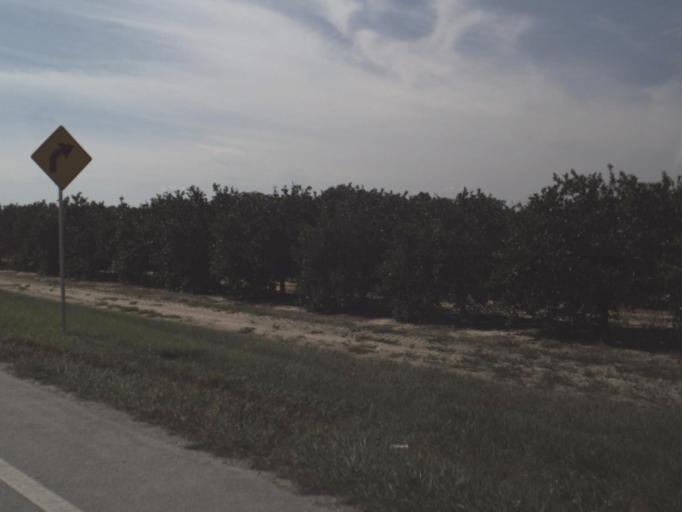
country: US
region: Florida
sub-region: Highlands County
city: Sebring
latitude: 27.5230
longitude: -81.4535
